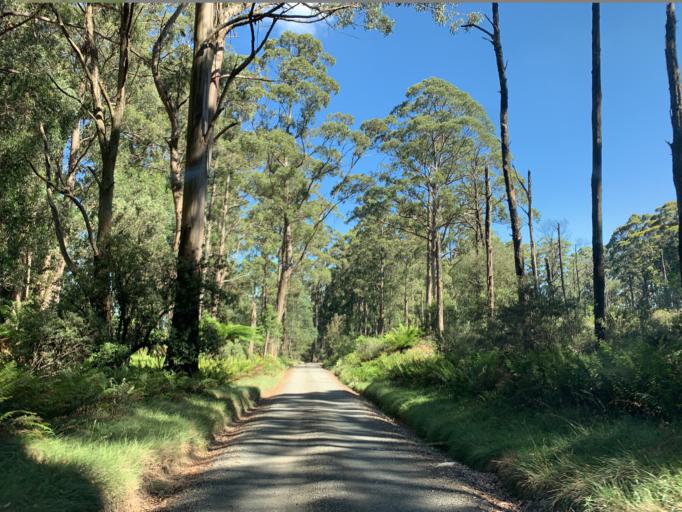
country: AU
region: Victoria
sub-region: Yarra Ranges
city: Millgrove
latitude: -37.7217
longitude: 145.6169
